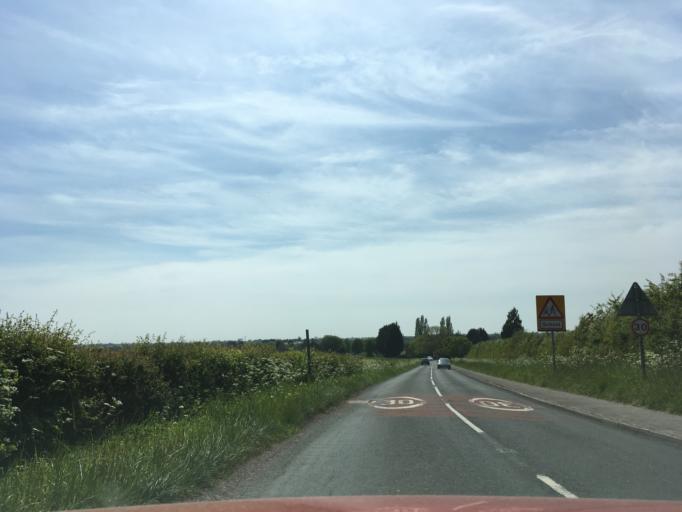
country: GB
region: England
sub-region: Gloucestershire
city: Wotton-under-Edge
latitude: 51.6331
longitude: -2.3607
